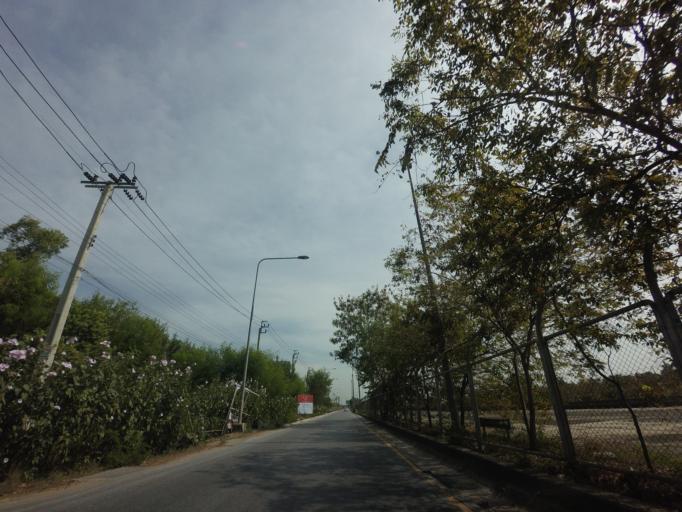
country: TH
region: Bangkok
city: Sai Mai
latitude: 13.8977
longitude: 100.6842
